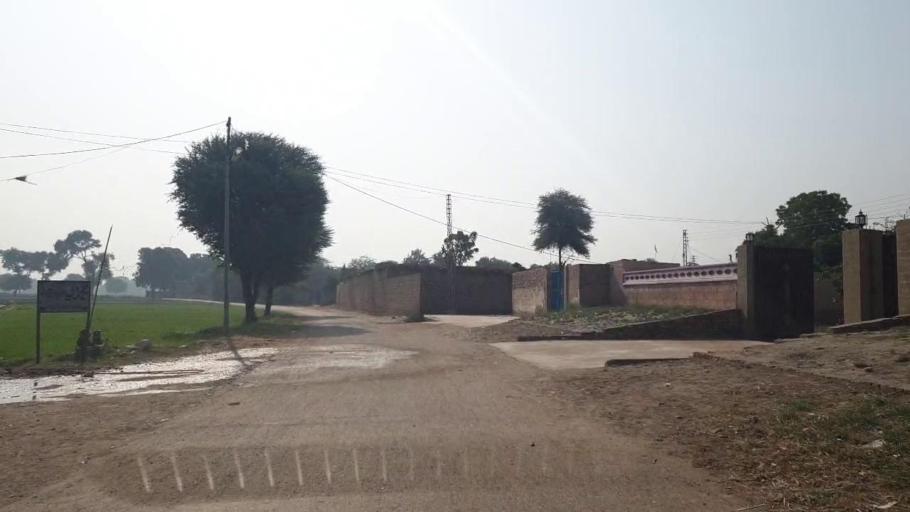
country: PK
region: Sindh
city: Kotri
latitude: 25.3566
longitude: 68.3080
